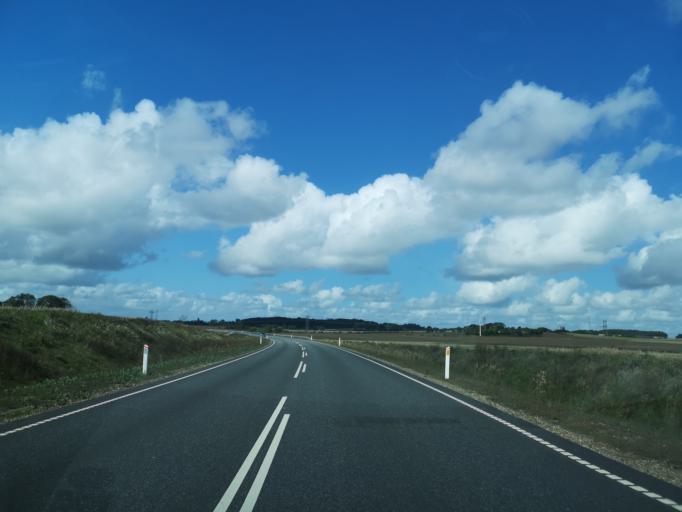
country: DK
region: Central Jutland
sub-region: Holstebro Kommune
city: Holstebro
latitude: 56.3947
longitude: 8.5780
